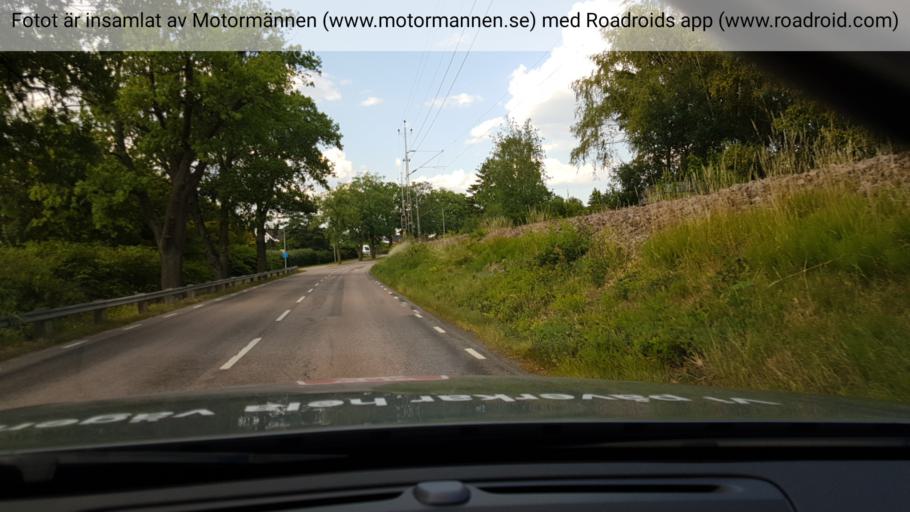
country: SE
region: Vaestmanland
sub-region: Vasteras
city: Tillberga
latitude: 59.6851
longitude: 16.6119
